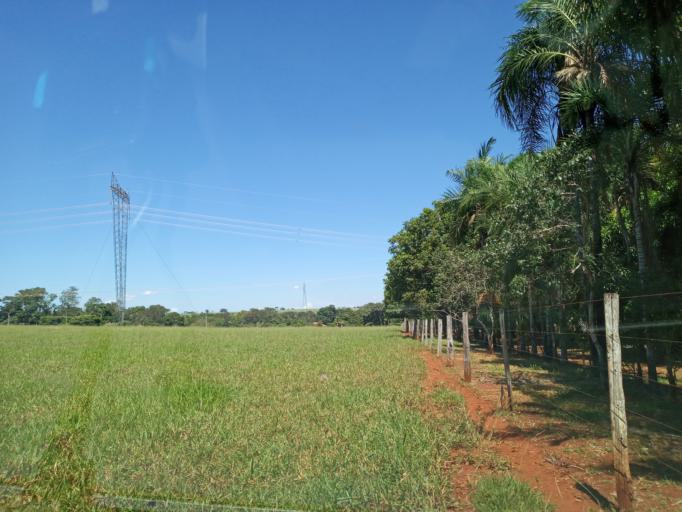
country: BR
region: Goias
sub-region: Itumbiara
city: Itumbiara
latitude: -18.3939
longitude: -49.1243
